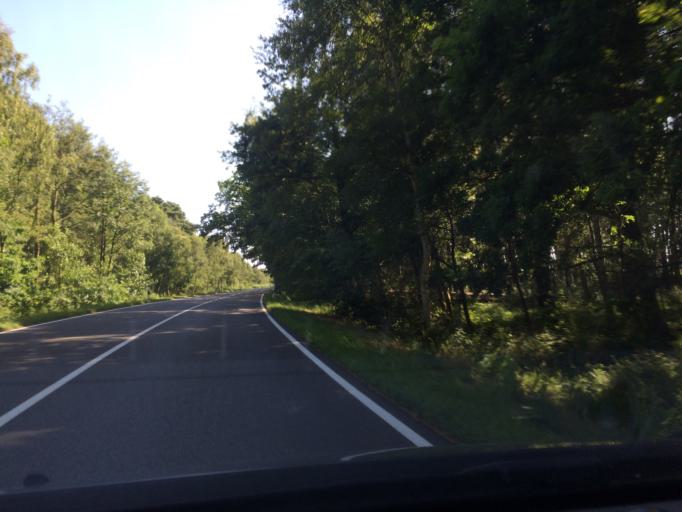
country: DE
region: Mecklenburg-Vorpommern
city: Zingst
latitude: 54.4346
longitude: 12.6522
